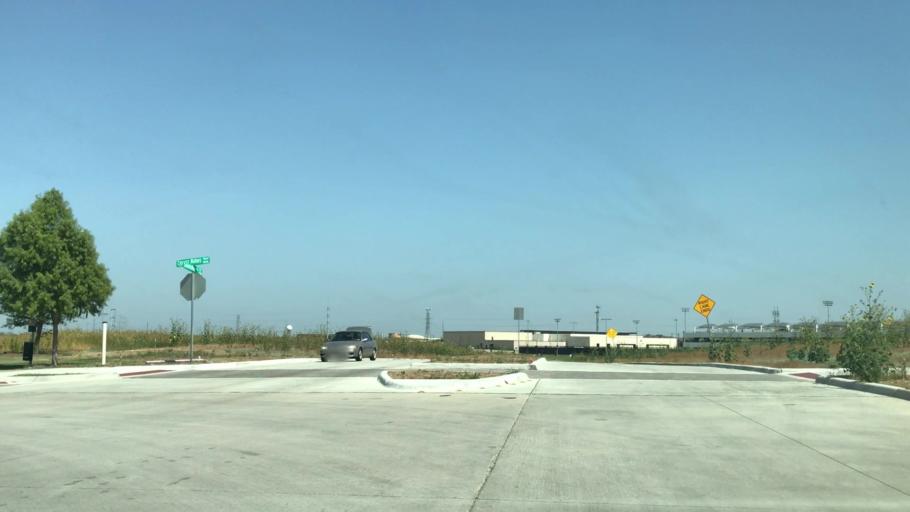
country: US
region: Texas
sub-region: Dallas County
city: Coppell
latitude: 32.9301
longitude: -96.9870
